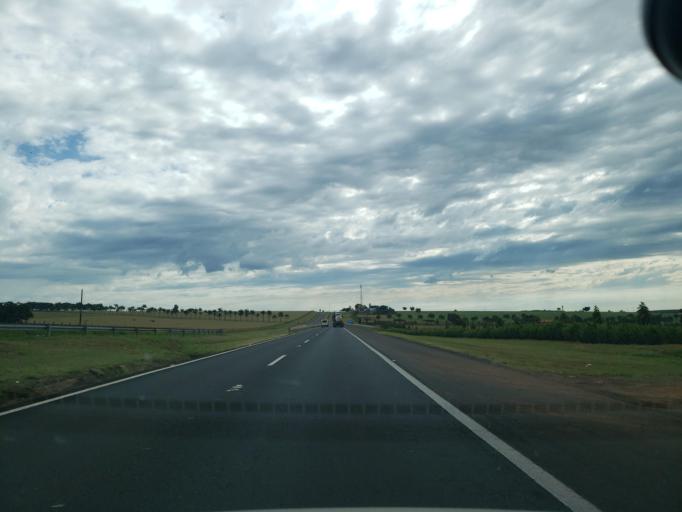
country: BR
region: Sao Paulo
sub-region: Bauru
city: Bauru
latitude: -22.1924
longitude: -49.2044
